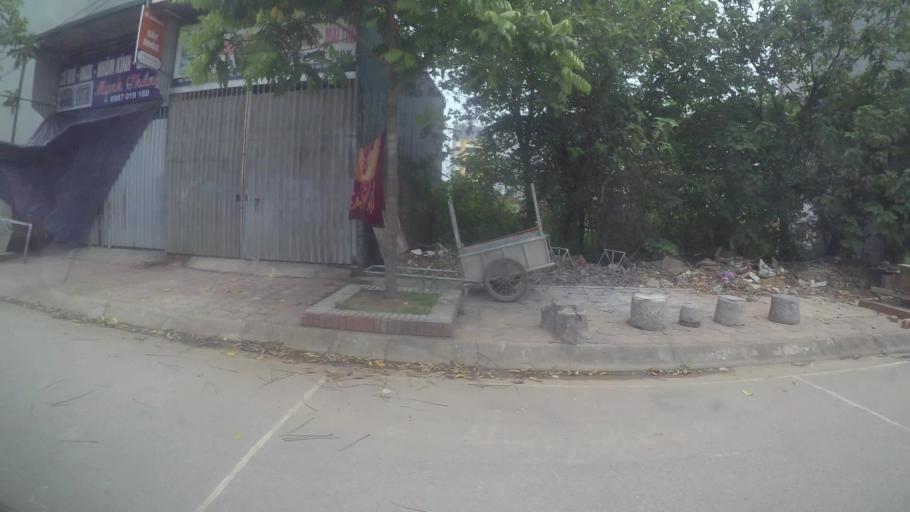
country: VN
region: Ha Noi
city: Ha Dong
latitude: 20.9898
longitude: 105.7426
